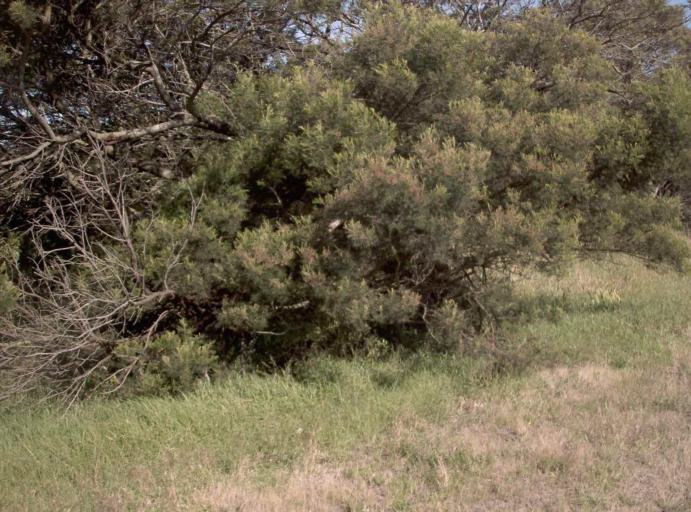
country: AU
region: Victoria
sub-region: Latrobe
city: Traralgon
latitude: -38.6219
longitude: 146.6729
